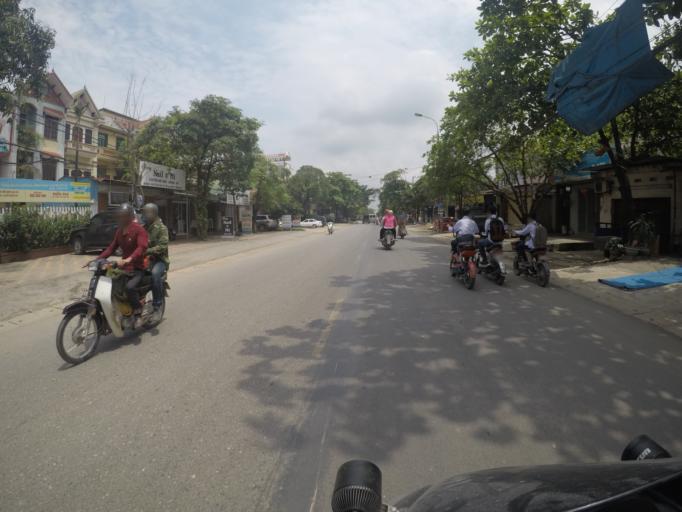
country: VN
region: Ha Noi
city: Soc Son
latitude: 21.2043
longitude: 105.8489
